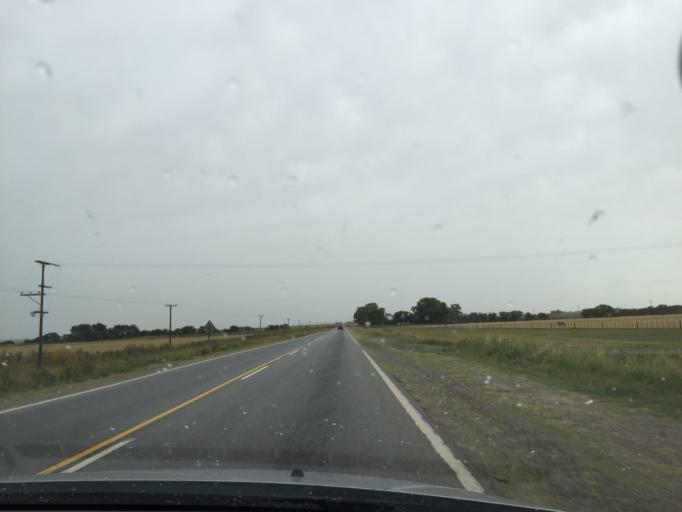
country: AR
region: Buenos Aires
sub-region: Partido de Tandil
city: Tandil
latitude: -37.5611
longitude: -58.7892
